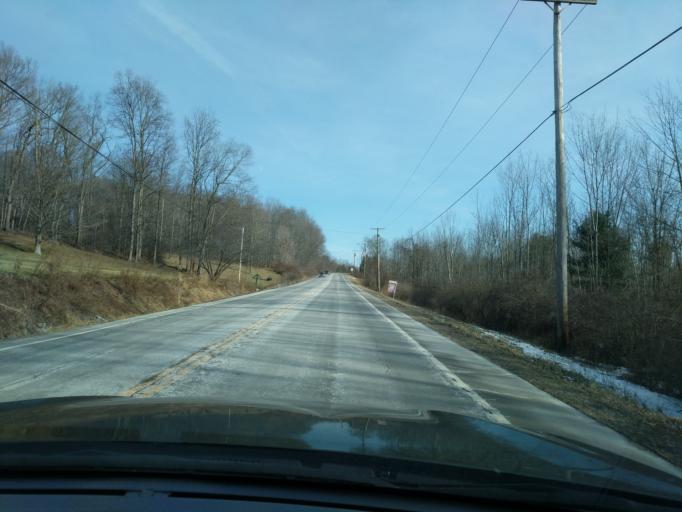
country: US
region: New York
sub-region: Tompkins County
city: East Ithaca
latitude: 42.3961
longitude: -76.4074
